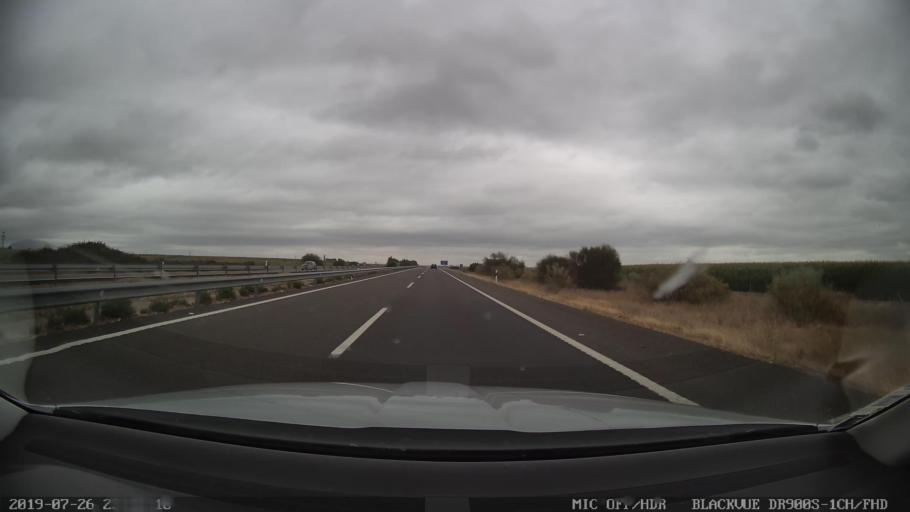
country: ES
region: Extremadura
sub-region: Provincia de Badajoz
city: Santa Amalia
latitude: 39.0670
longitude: -6.0482
